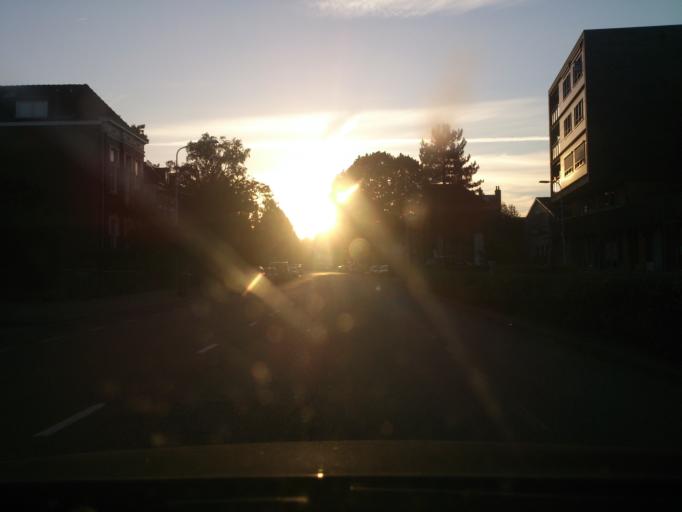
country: NL
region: Gelderland
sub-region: Gemeente Nijmegen
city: Nijmegen
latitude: 51.8492
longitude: 5.8507
